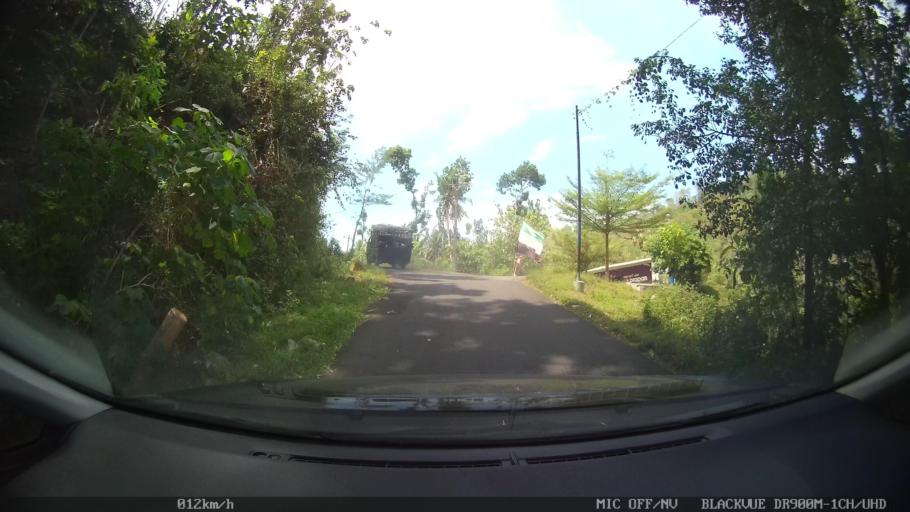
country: ID
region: Central Java
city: Candi Prambanan
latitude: -7.8156
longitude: 110.5145
